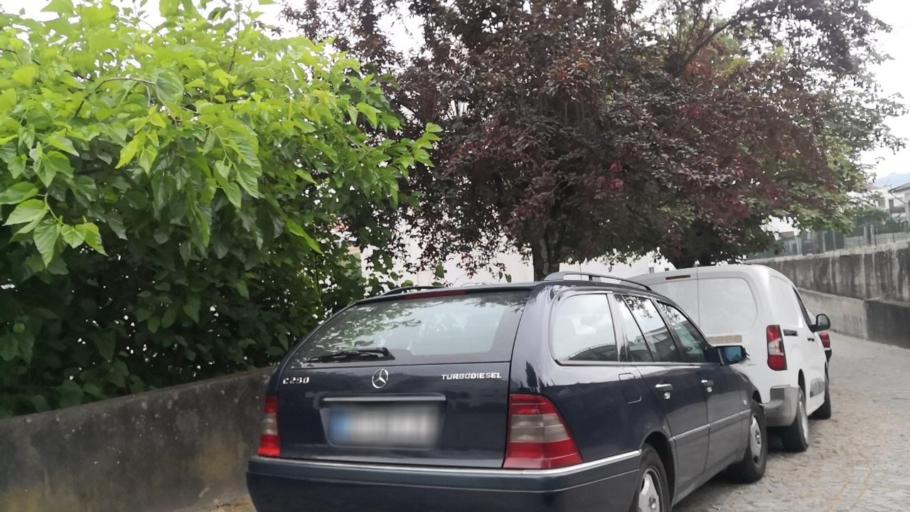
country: PT
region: Porto
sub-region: Amarante
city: Amarante
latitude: 41.2689
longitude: -8.0717
